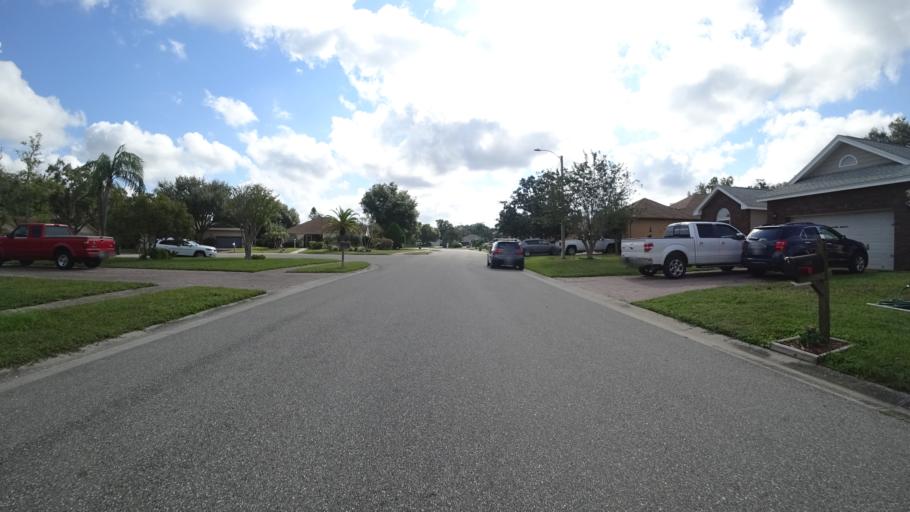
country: US
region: Florida
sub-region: Sarasota County
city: North Sarasota
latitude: 27.4085
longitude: -82.5075
